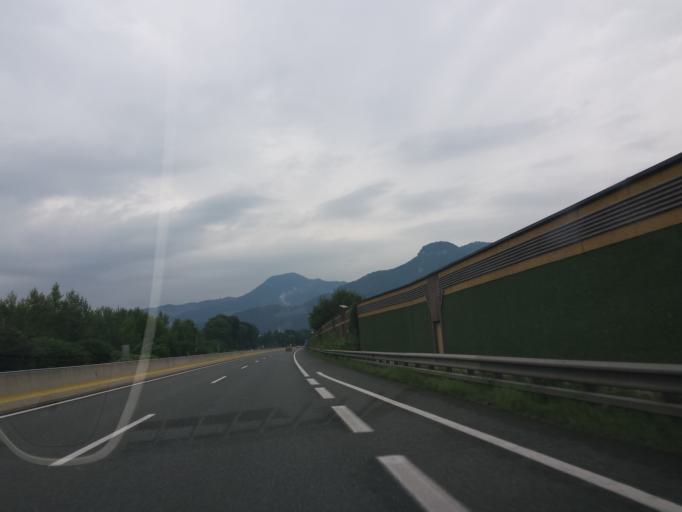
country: AT
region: Styria
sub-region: Politischer Bezirk Graz-Umgebung
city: Frohnleiten
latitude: 47.2530
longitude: 15.3169
